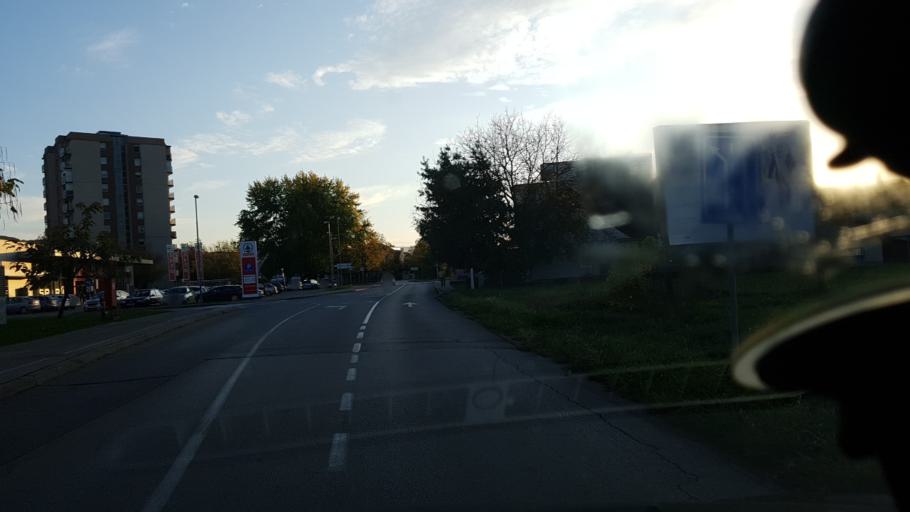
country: SI
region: Brezice
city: Brezice
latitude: 45.9096
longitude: 15.5975
